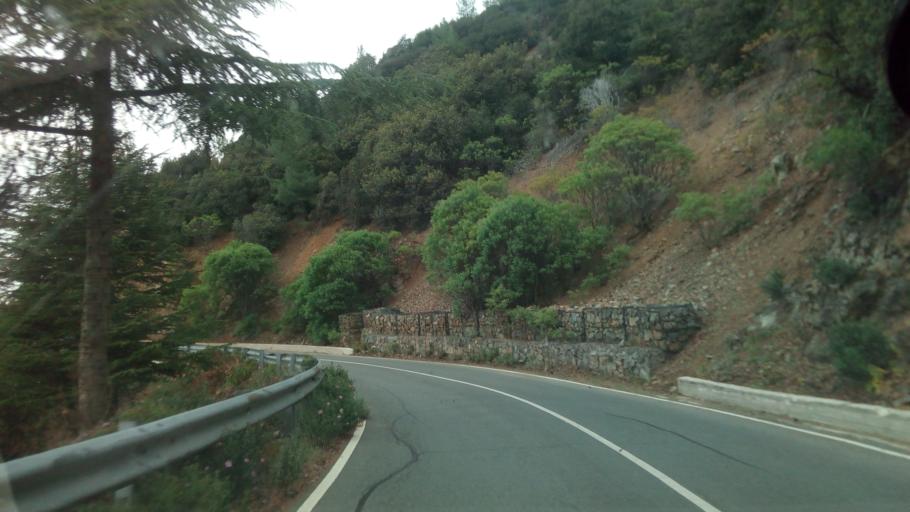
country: CY
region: Lefkosia
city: Kato Pyrgos
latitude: 34.9987
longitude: 32.7041
